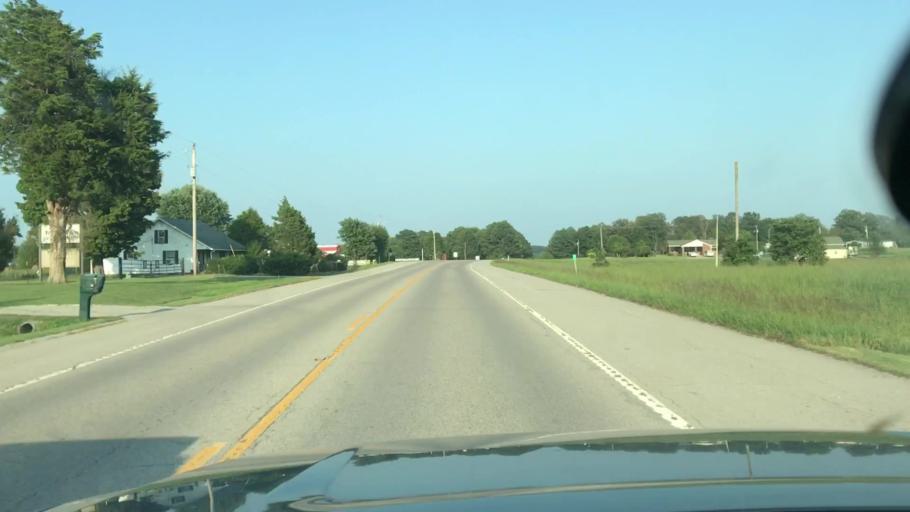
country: US
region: Tennessee
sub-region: Sumner County
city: Portland
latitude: 36.5785
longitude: -86.4360
